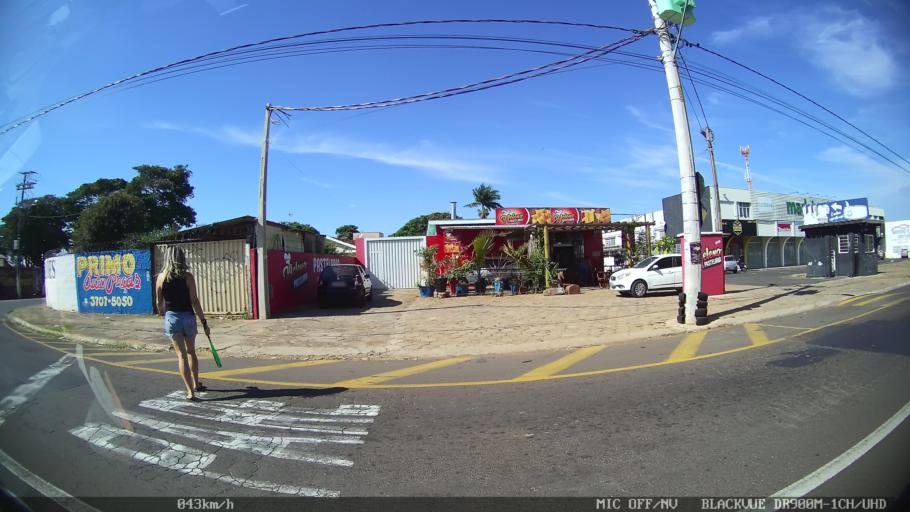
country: BR
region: Sao Paulo
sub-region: Franca
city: Franca
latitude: -20.4886
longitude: -47.3985
